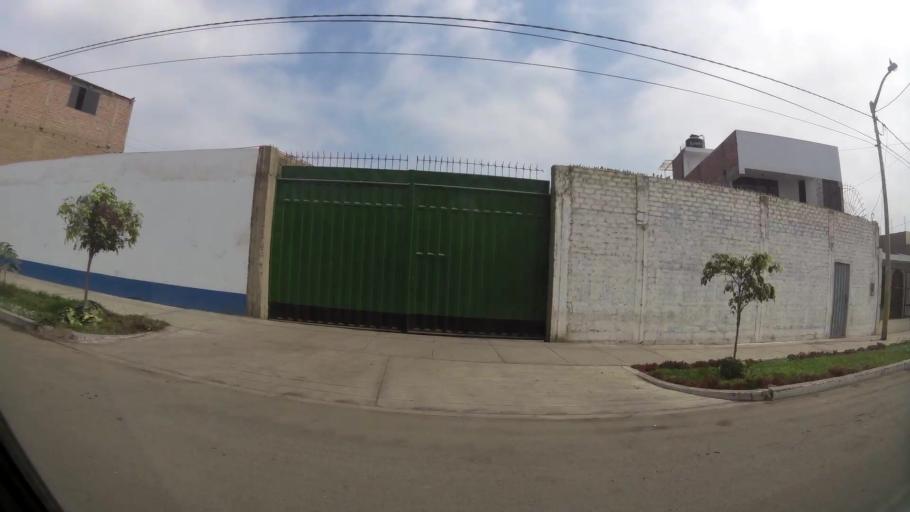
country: PE
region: Lima
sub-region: Provincia de Huaral
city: Huaral
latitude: -11.4957
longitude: -77.2153
